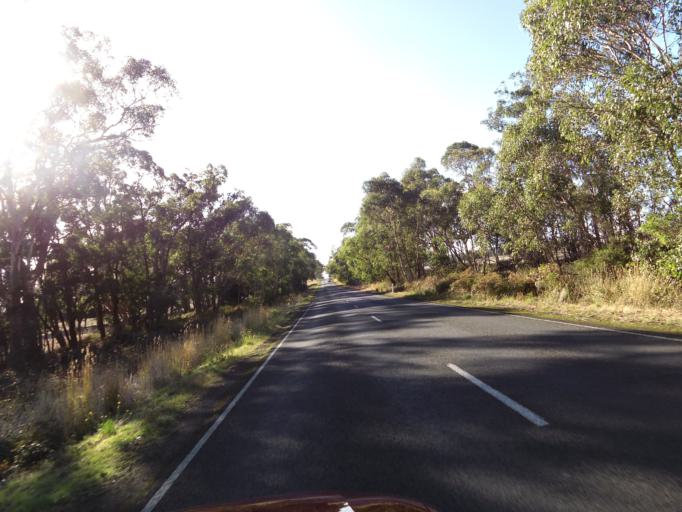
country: AU
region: Victoria
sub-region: Warrnambool
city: Allansford
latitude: -38.3915
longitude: 142.8923
